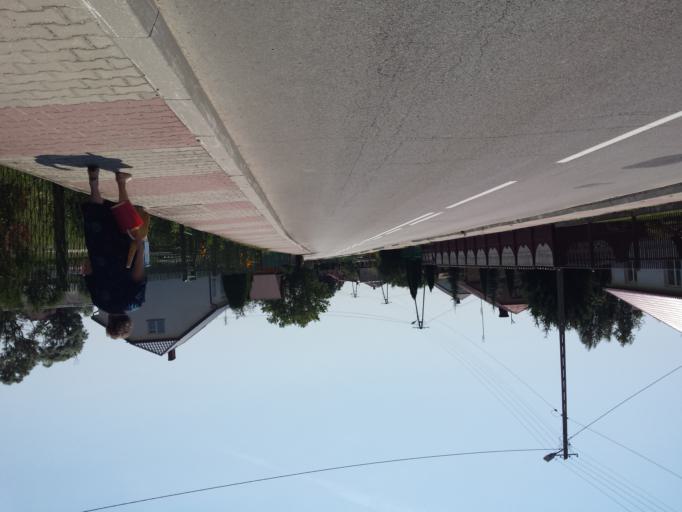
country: PL
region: Lublin Voivodeship
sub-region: Powiat bialski
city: Koden
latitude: 51.9028
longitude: 23.6007
